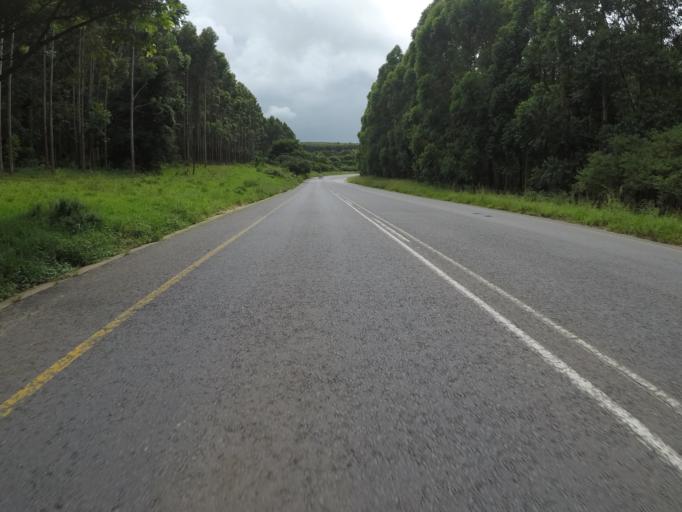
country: ZA
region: KwaZulu-Natal
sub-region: uThungulu District Municipality
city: eSikhawini
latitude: -28.8649
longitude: 31.8907
